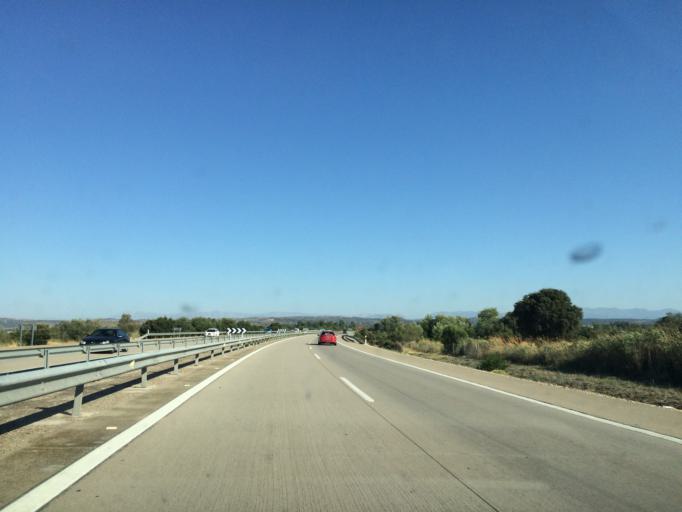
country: ES
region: Castille-La Mancha
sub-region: Province of Toledo
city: Talavera de la Reina
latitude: 39.9837
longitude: -4.7535
